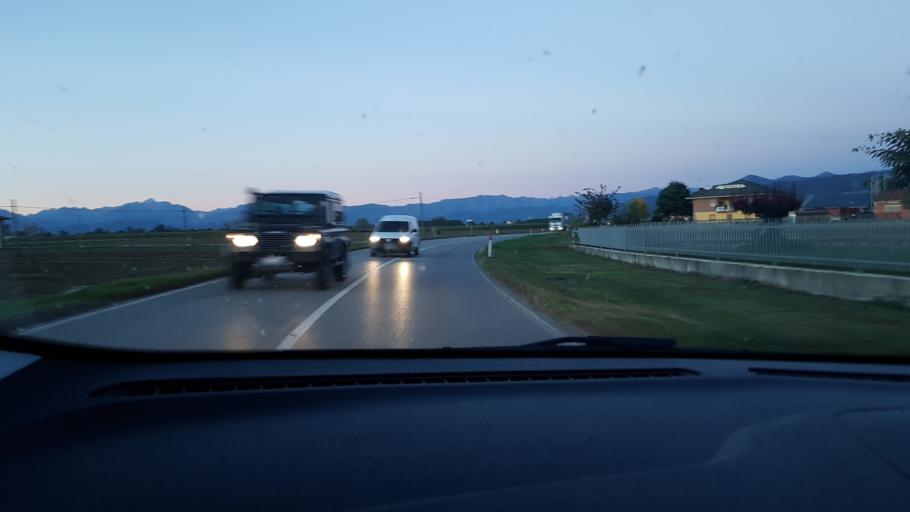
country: IT
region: Piedmont
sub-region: Provincia di Cuneo
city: Vottignasco
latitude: 44.5570
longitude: 7.5637
